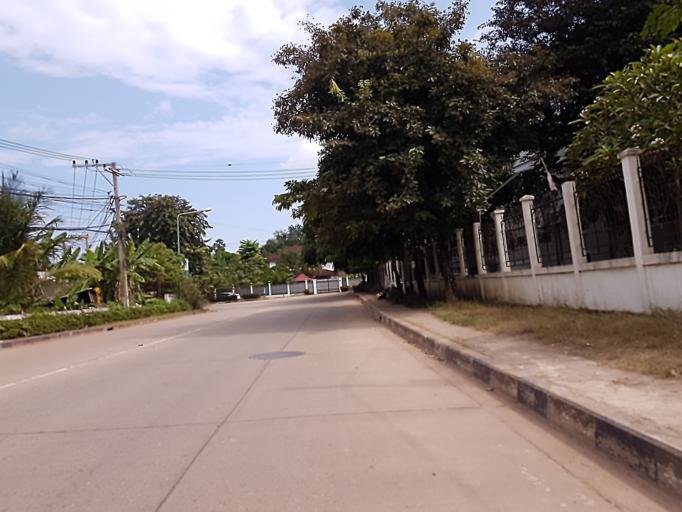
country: LA
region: Vientiane
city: Vientiane
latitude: 17.9389
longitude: 102.6192
